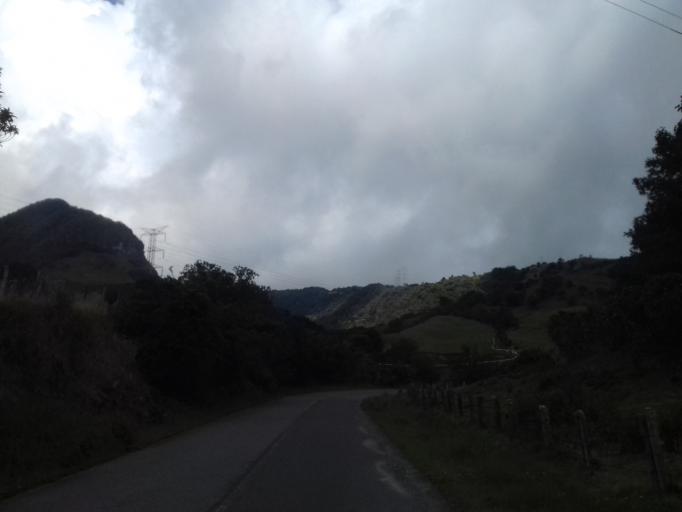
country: CO
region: Tolima
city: Herveo
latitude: 5.0155
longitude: -75.3314
